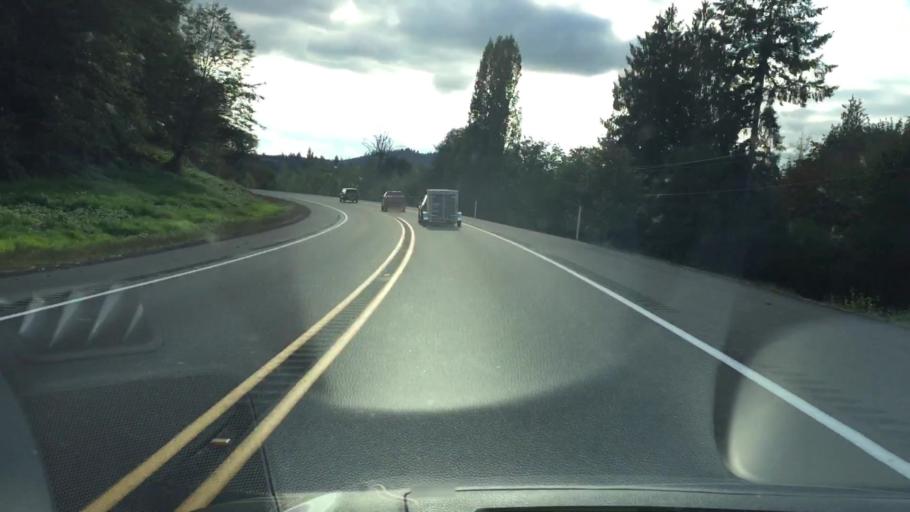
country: US
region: Washington
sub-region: Lewis County
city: Morton
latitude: 46.5361
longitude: -122.5457
